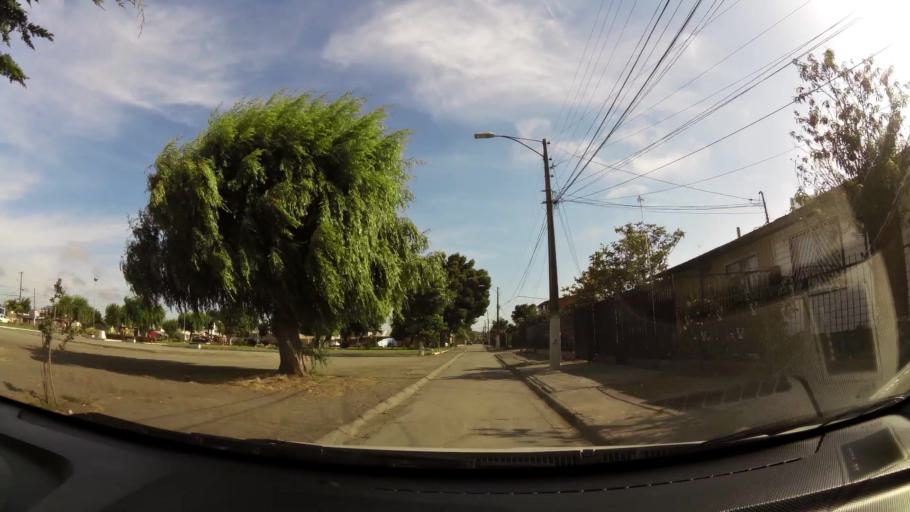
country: CL
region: Biobio
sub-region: Provincia de Concepcion
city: Talcahuano
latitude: -36.7854
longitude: -73.1147
